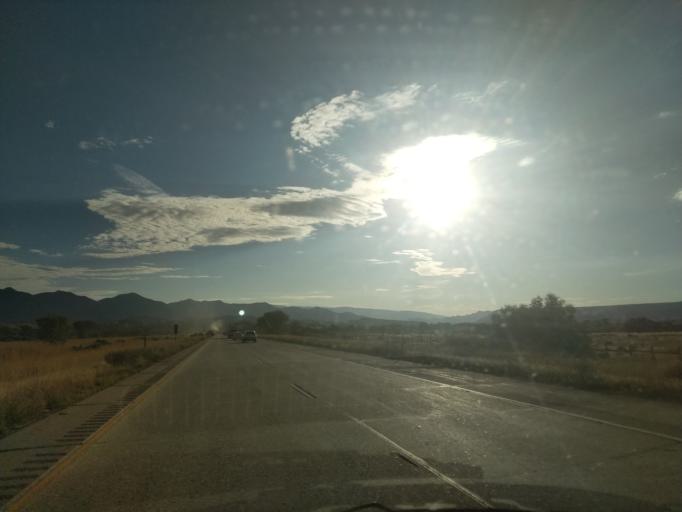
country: US
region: Colorado
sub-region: Garfield County
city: Silt
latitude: 39.5387
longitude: -107.6809
